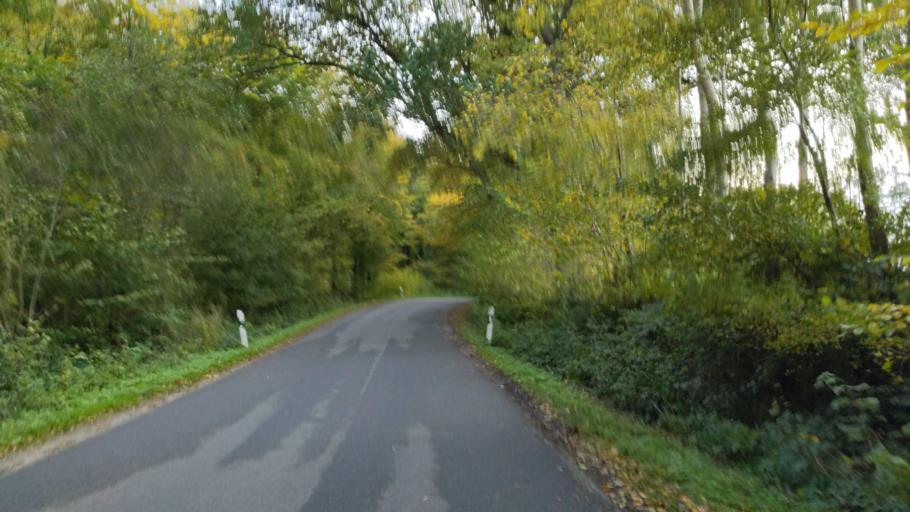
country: DE
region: Schleswig-Holstein
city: Susel
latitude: 54.0539
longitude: 10.7209
